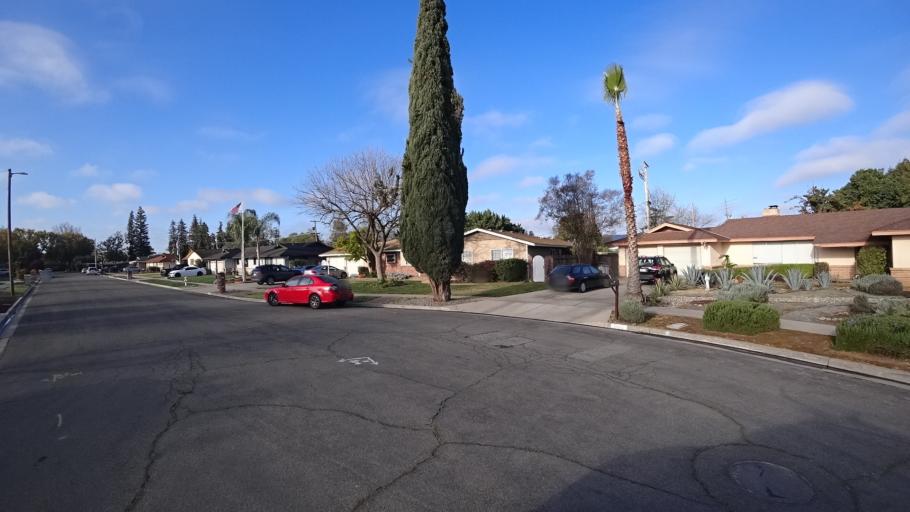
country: US
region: California
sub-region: Fresno County
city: Fresno
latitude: 36.8207
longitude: -119.7967
